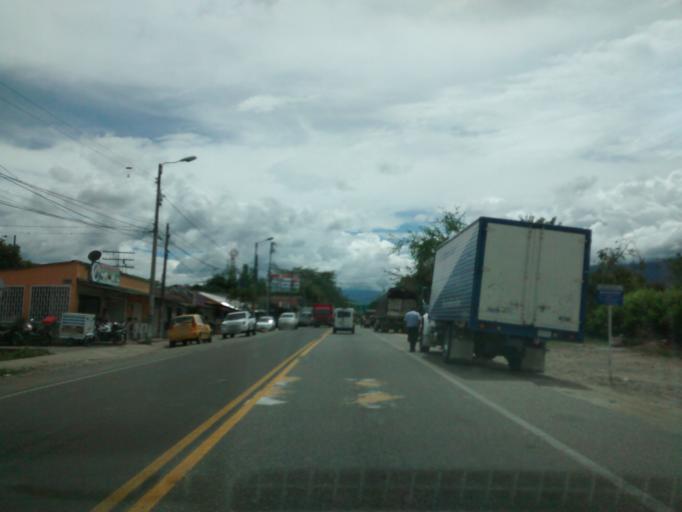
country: CO
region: Tolima
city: Ibague
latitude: 4.3985
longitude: -75.1426
